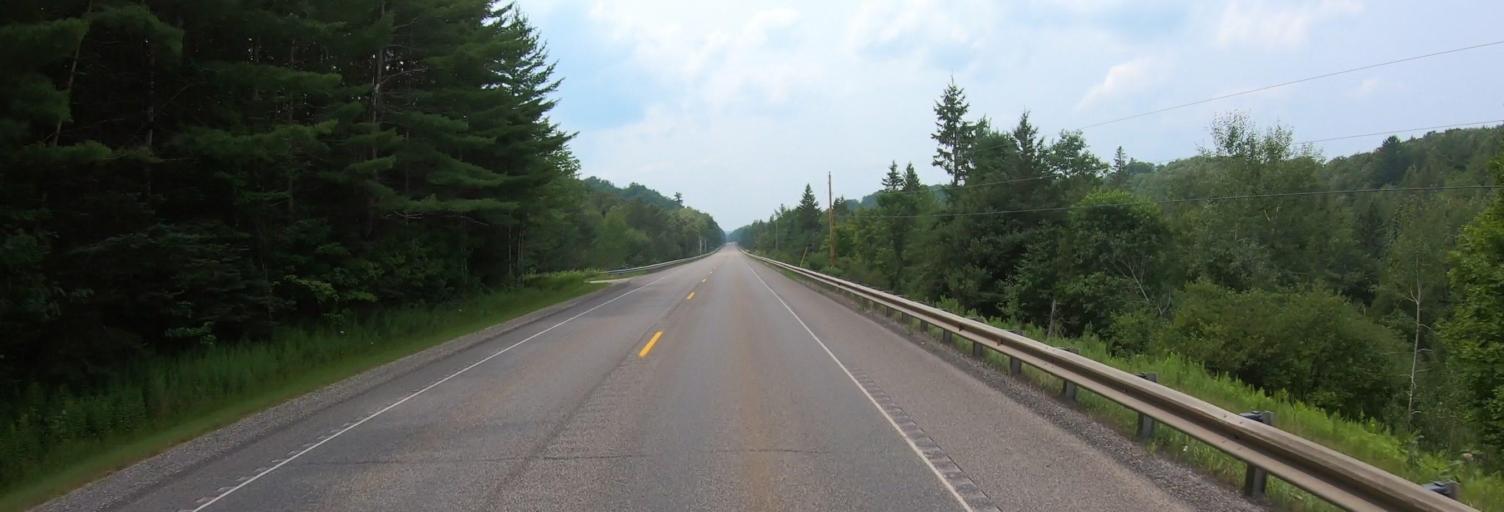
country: US
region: Michigan
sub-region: Alger County
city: Munising
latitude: 46.3878
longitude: -86.6550
